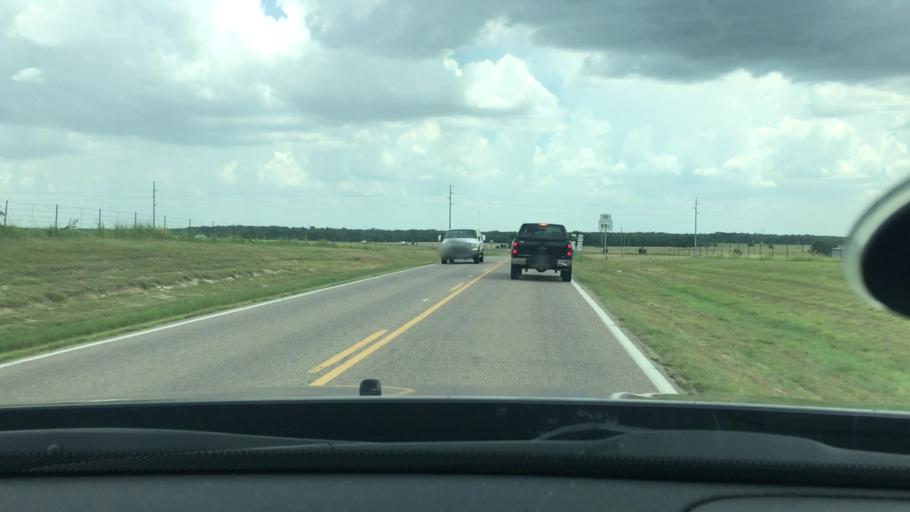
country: US
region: Oklahoma
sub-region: Marshall County
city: Oakland
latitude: 34.0709
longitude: -96.8009
